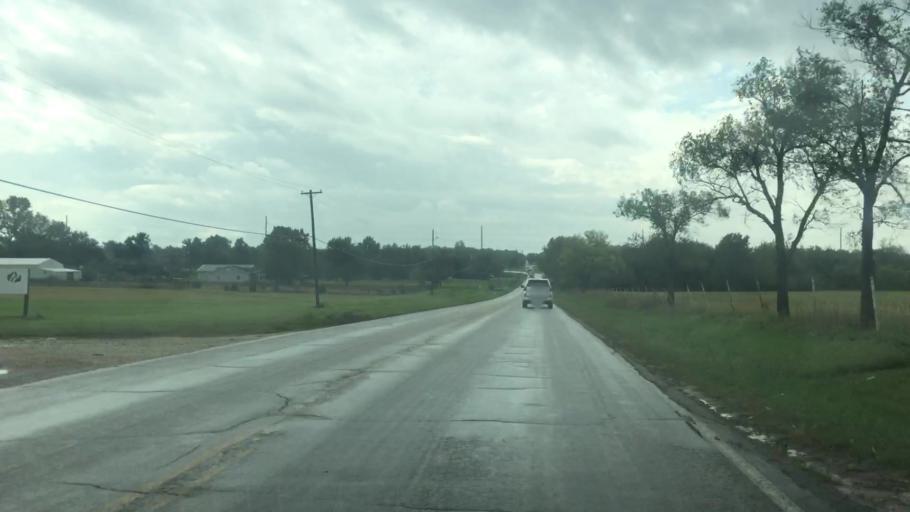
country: US
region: Kansas
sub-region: Allen County
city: Iola
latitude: 37.8965
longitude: -95.4094
